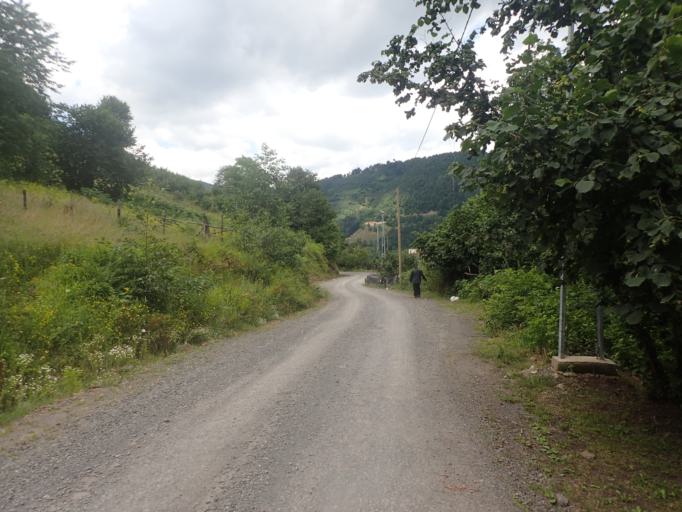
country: TR
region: Ordu
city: Akkus
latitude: 40.8987
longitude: 37.0104
